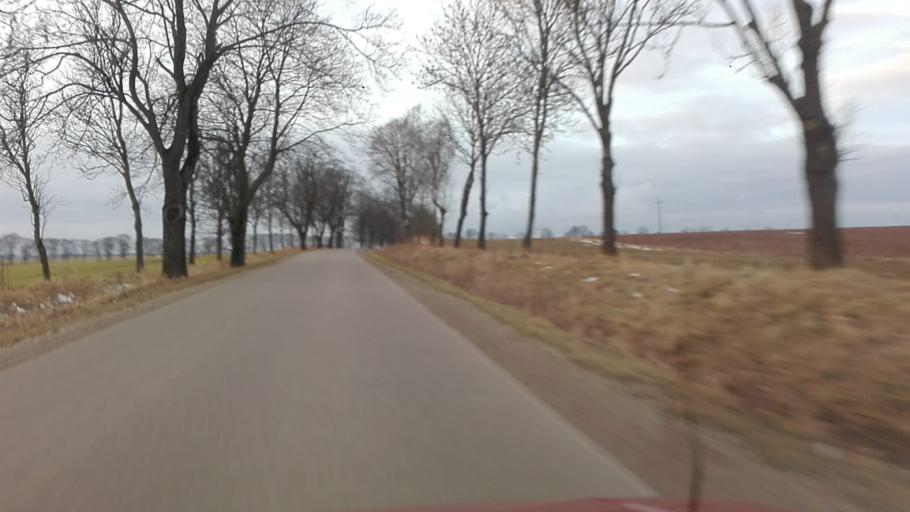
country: PL
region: West Pomeranian Voivodeship
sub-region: Powiat swidwinski
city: Rabino
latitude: 53.8015
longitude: 15.9108
